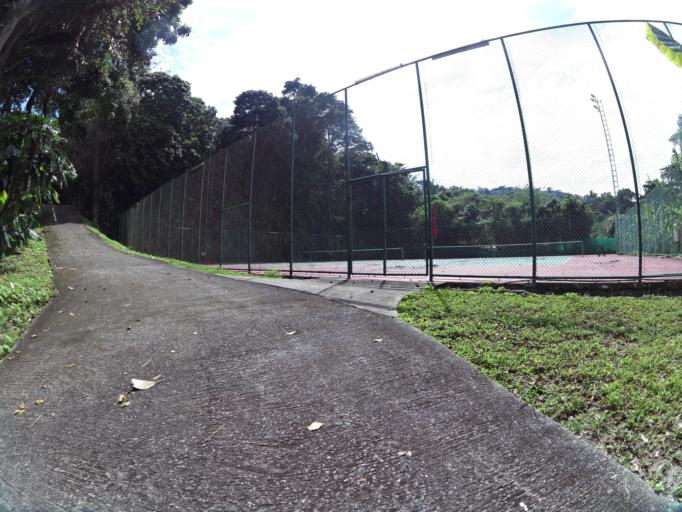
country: TH
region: Phuket
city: Patong
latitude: 7.8862
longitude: 98.2794
